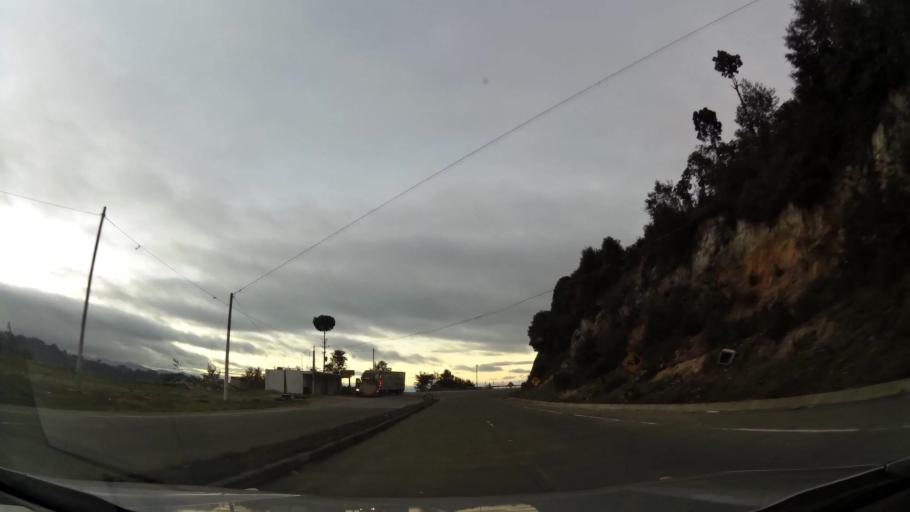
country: GT
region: Solola
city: Concepcion
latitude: 14.8359
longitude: -91.0742
